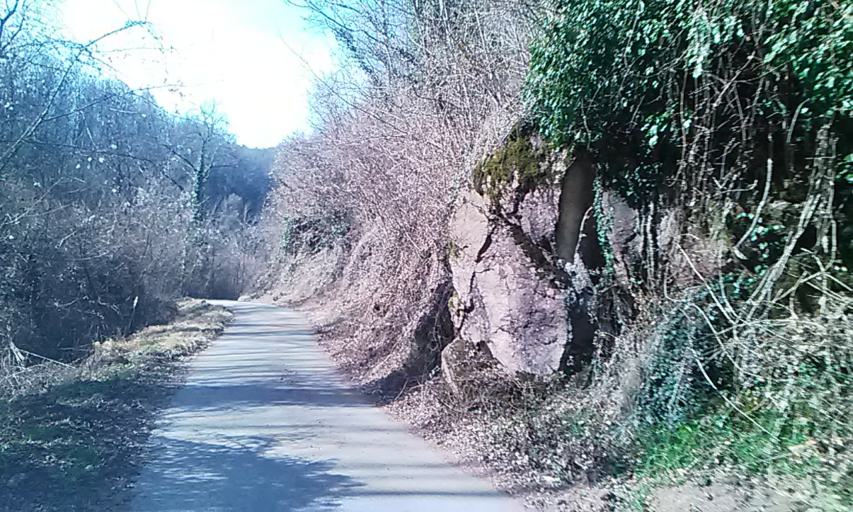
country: IT
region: Piedmont
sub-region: Provincia di Biella
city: Sostegno
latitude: 45.6545
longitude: 8.2589
